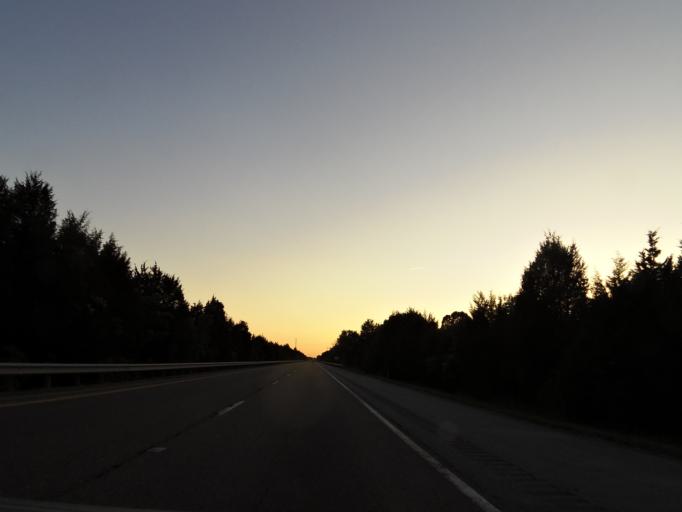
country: US
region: Tennessee
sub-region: Greene County
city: Mosheim
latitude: 36.2043
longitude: -83.1014
